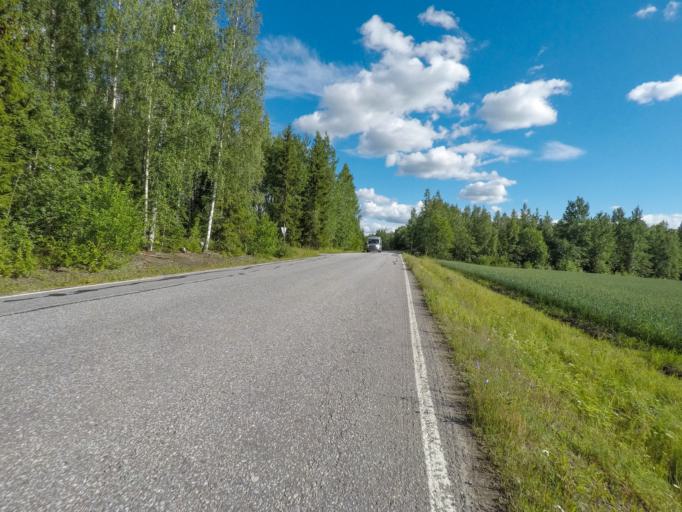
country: FI
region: South Karelia
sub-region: Imatra
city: Imatra
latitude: 61.1328
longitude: 28.6606
